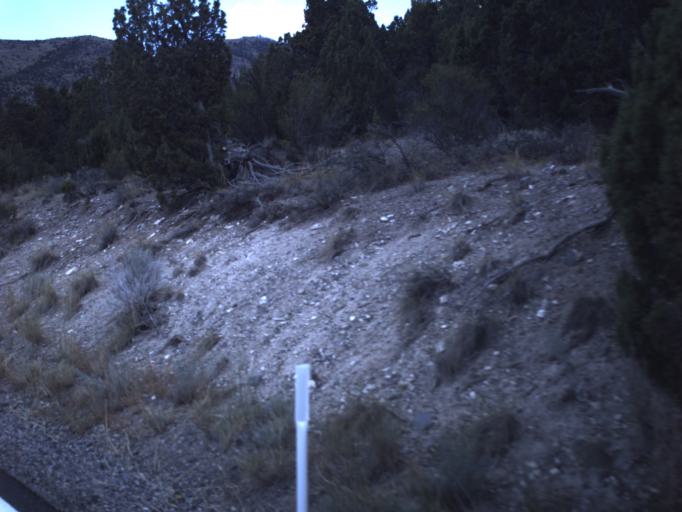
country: US
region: Utah
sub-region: Tooele County
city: Grantsville
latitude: 40.3483
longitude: -112.5552
